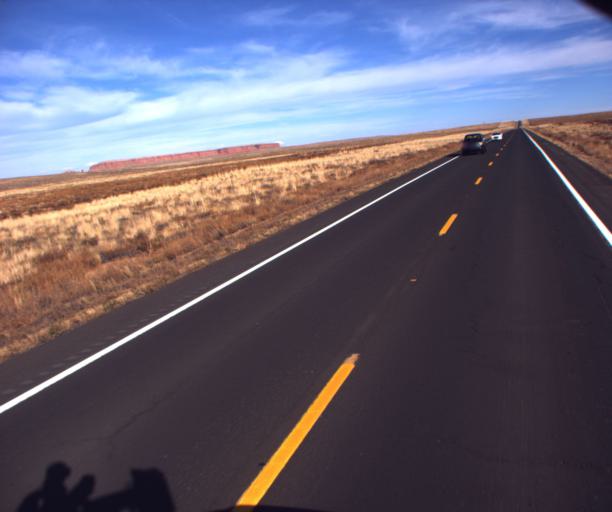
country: US
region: Arizona
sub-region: Apache County
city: Lukachukai
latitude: 36.9624
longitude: -109.4299
